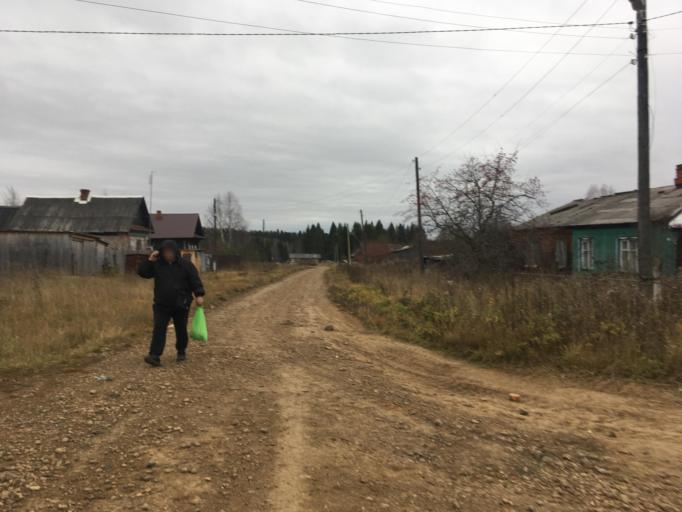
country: RU
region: Perm
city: Komarikhinskiy
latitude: 58.0898
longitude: 57.1101
